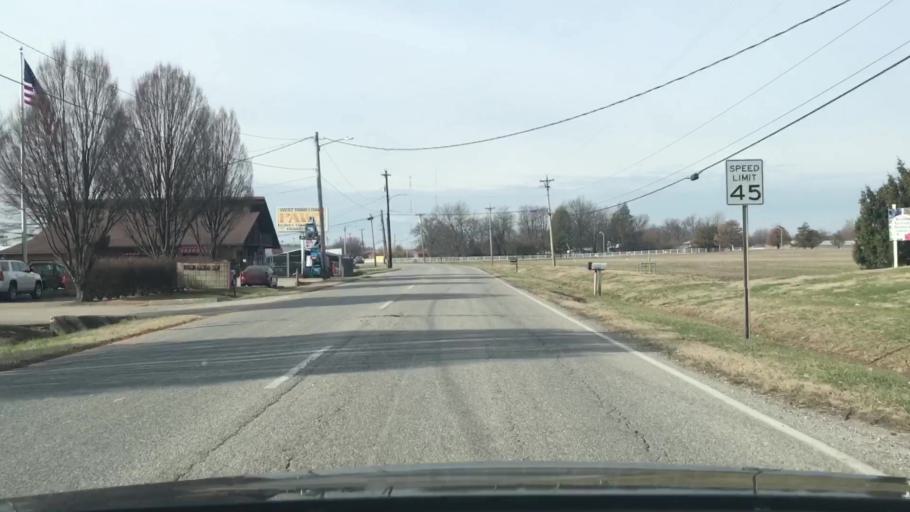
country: US
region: Kentucky
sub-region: Daviess County
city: Owensboro
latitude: 37.7739
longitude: -87.1454
